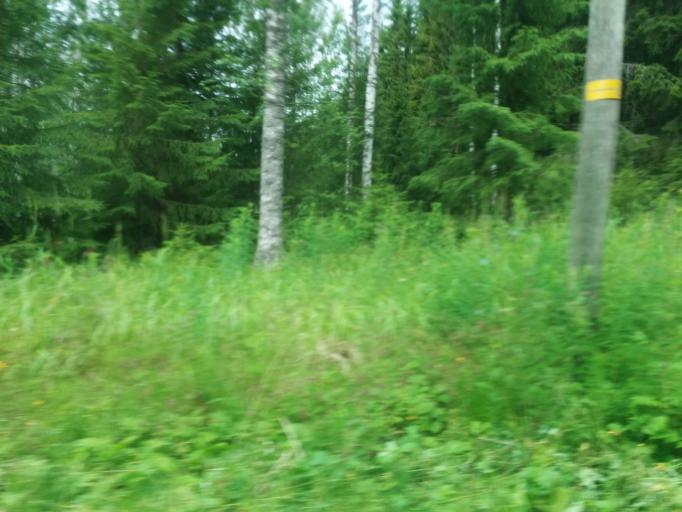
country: FI
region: Pirkanmaa
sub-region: Tampere
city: Kuhmalahti
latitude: 61.6867
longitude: 24.5710
